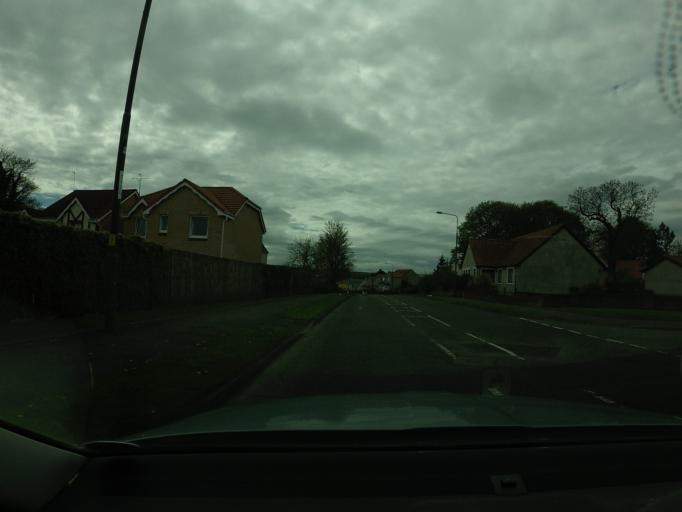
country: GB
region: Scotland
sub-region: West Lothian
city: Broxburn
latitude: 55.9358
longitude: -3.4817
